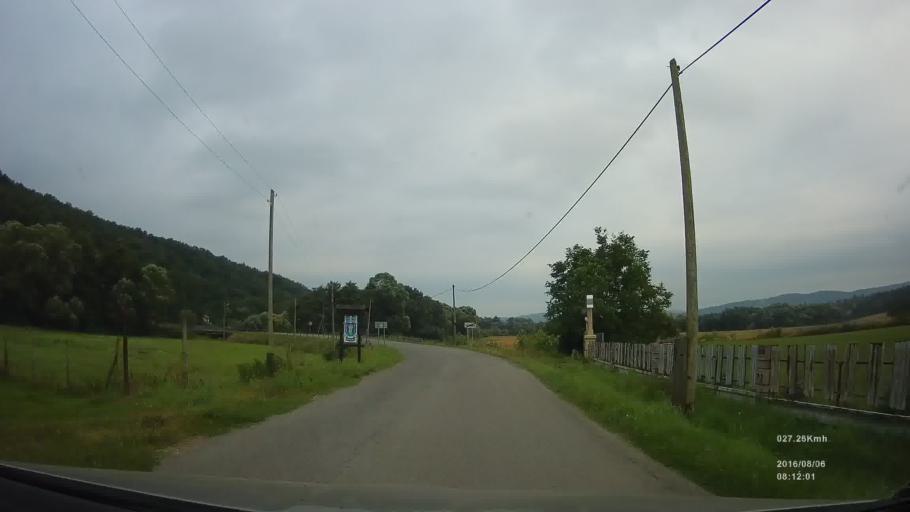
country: SK
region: Presovsky
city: Stropkov
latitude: 49.2272
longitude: 21.6627
